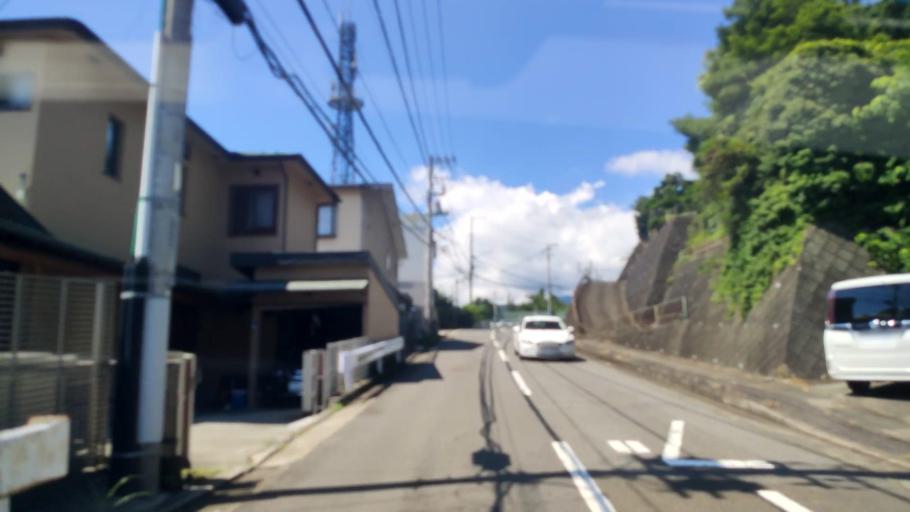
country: JP
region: Kanagawa
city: Odawara
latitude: 35.2525
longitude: 139.1400
